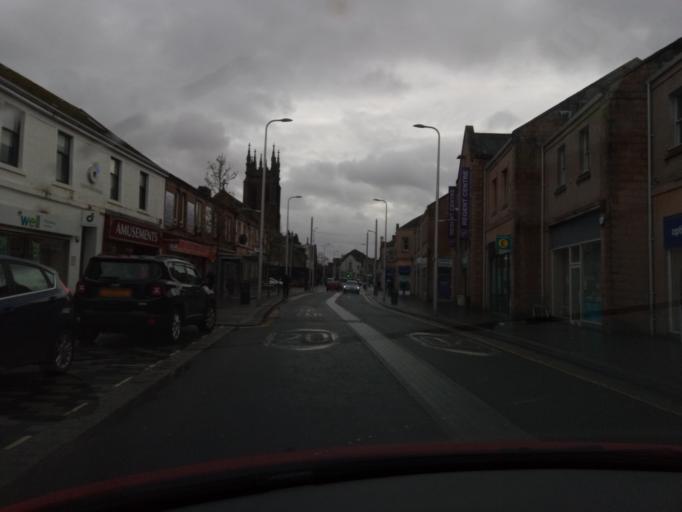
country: GB
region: Scotland
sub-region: East Dunbartonshire
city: Kirkintilloch
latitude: 55.9398
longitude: -4.1571
